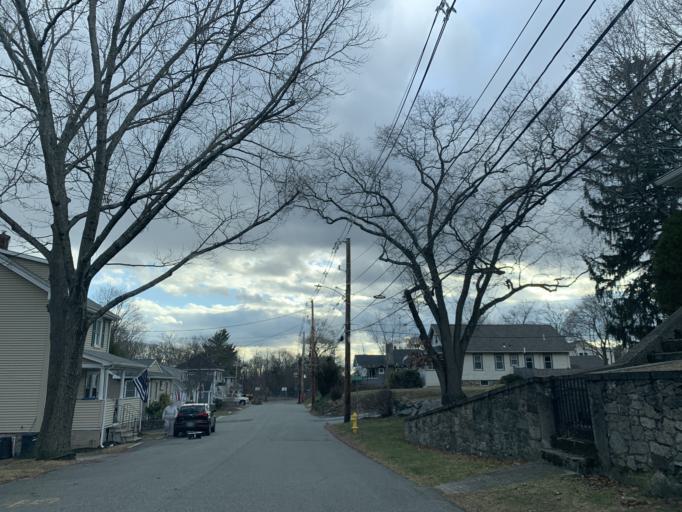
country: US
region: Massachusetts
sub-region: Norfolk County
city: Dedham
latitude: 42.2206
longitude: -71.1862
